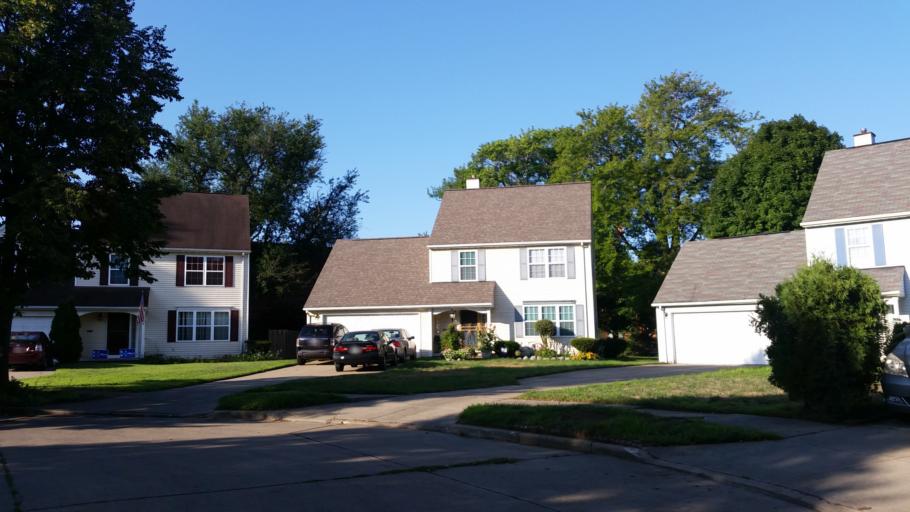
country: US
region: Ohio
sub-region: Cuyahoga County
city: Bratenahl
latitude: 41.5416
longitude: -81.6148
